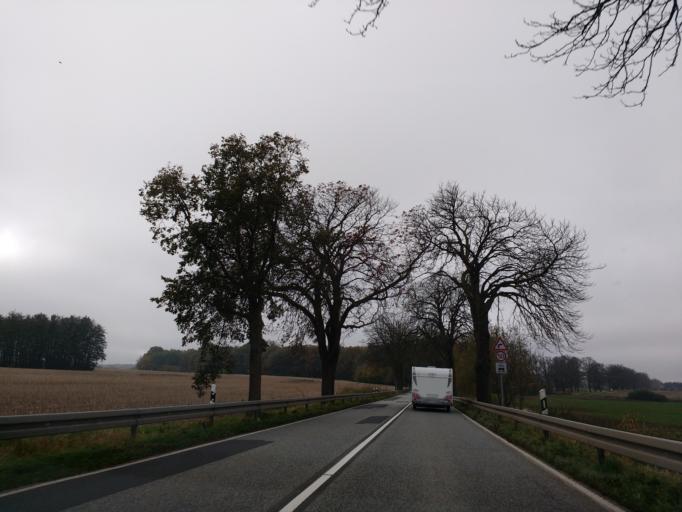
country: DE
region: Mecklenburg-Vorpommern
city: Dassow
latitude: 53.8966
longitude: 10.9312
